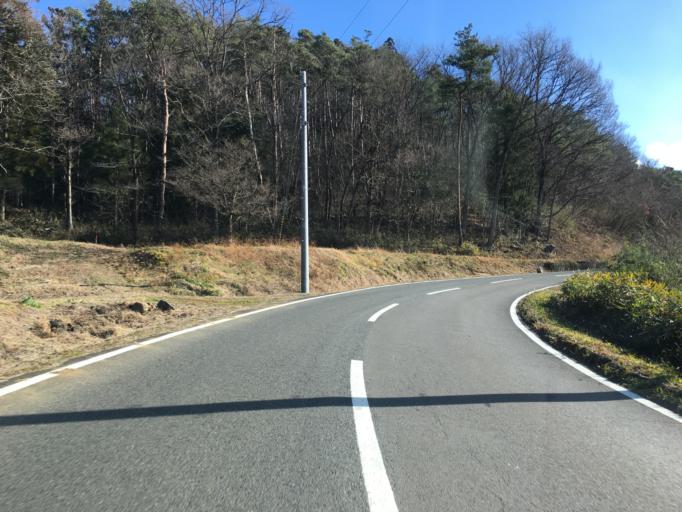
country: JP
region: Fukushima
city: Nihommatsu
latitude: 37.5854
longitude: 140.3961
